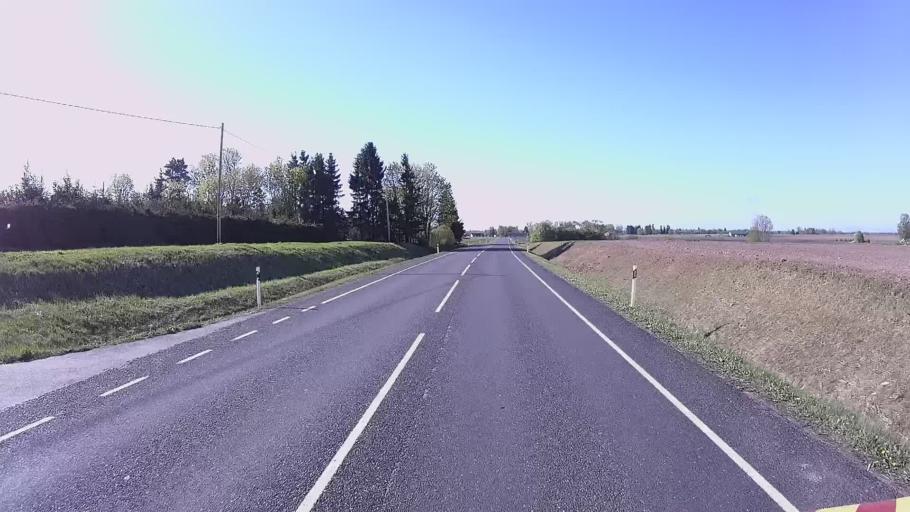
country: EE
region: Viljandimaa
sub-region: Vohma linn
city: Vohma
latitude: 58.6674
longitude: 25.6073
